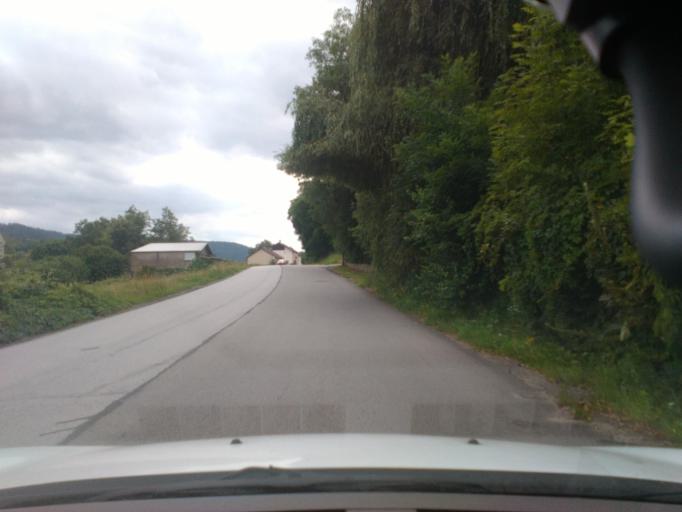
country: FR
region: Lorraine
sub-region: Departement des Vosges
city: Bruyeres
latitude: 48.1782
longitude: 6.6783
